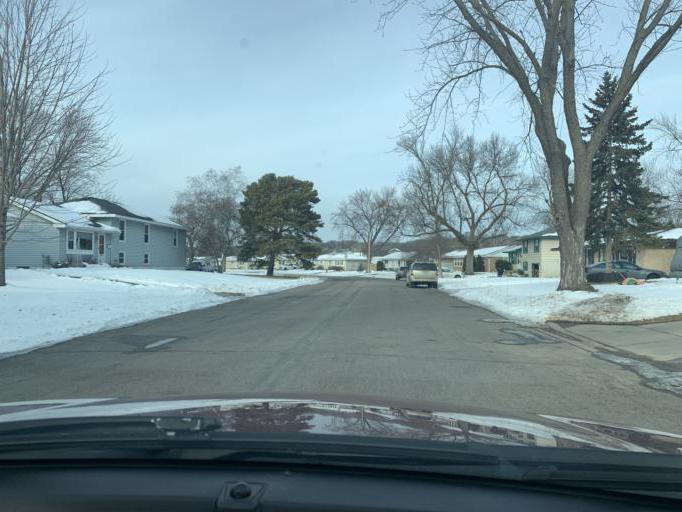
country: US
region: Minnesota
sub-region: Washington County
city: Saint Paul Park
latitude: 44.8369
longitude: -92.9753
